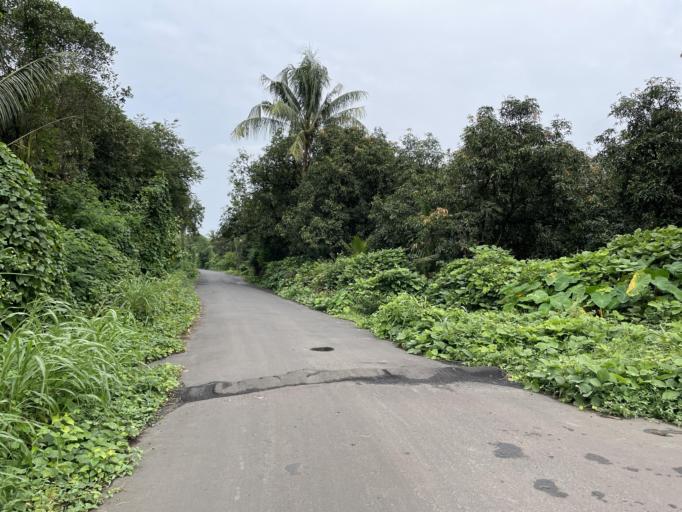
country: IN
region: Gujarat
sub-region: Valsad
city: Pardi
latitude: 20.4515
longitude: 72.9351
